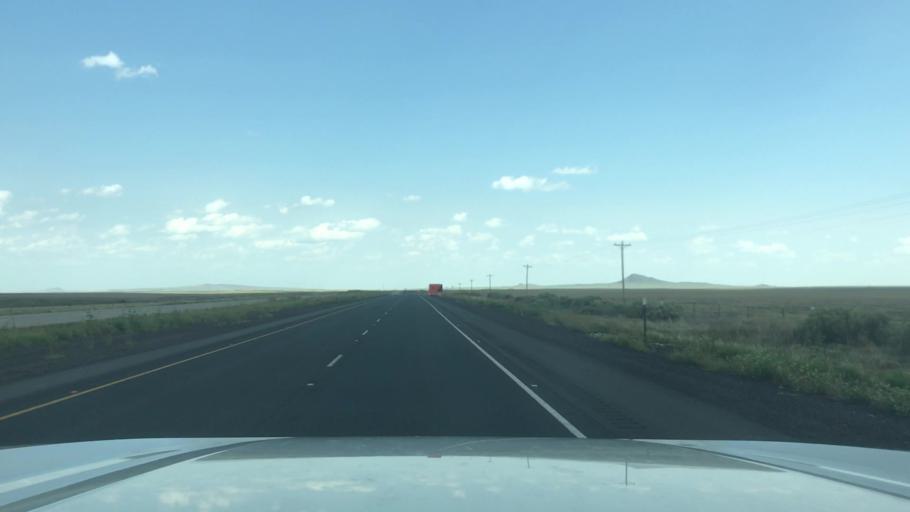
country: US
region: New Mexico
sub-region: Union County
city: Clayton
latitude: 36.6308
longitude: -103.7132
